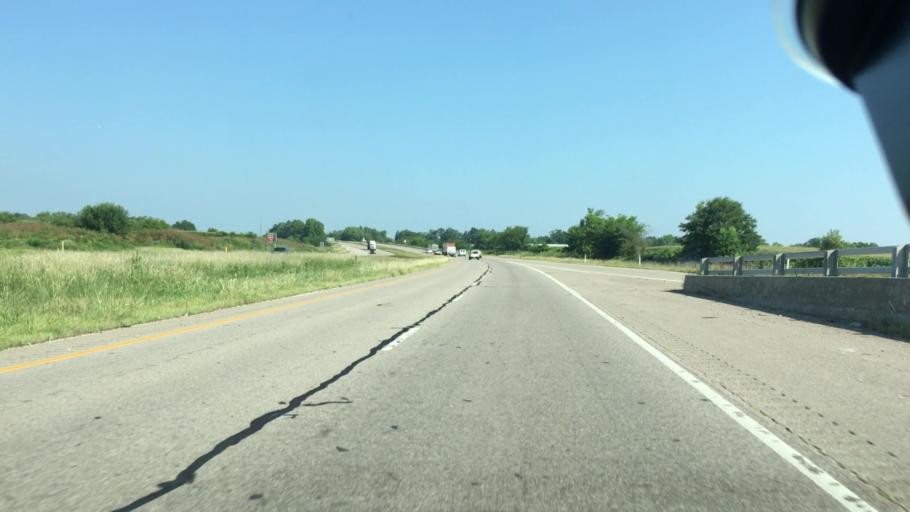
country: US
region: Indiana
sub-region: Gibson County
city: Princeton
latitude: 38.3143
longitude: -87.5694
